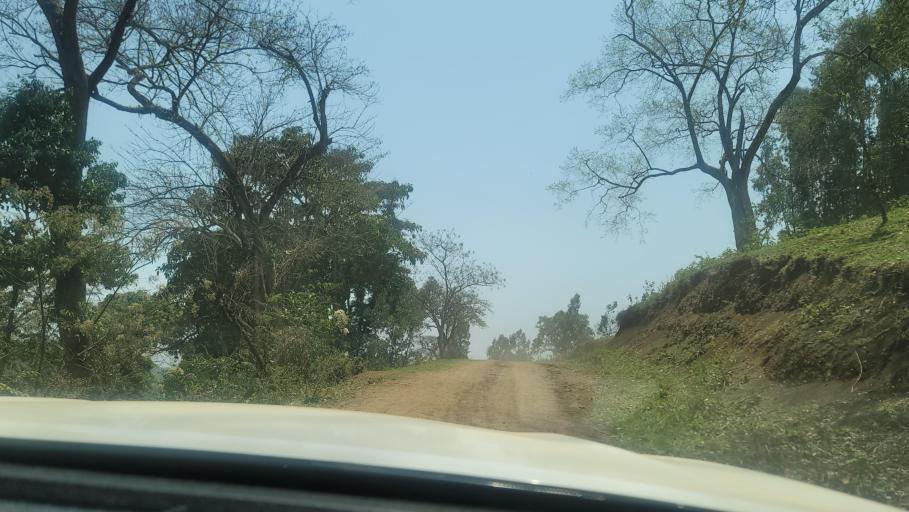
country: ET
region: Southern Nations, Nationalities, and People's Region
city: Bonga
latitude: 7.5280
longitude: 36.1981
